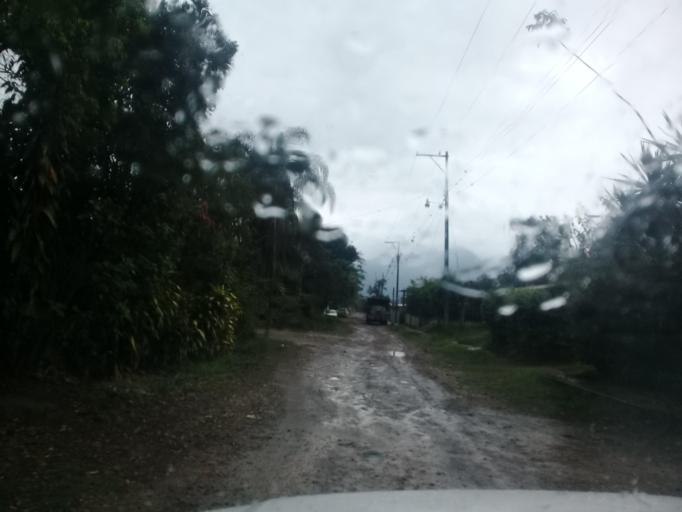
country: MX
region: Veracruz
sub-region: Amatlan de los Reyes
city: Trapiche Viejo
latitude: 18.8425
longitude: -96.9481
